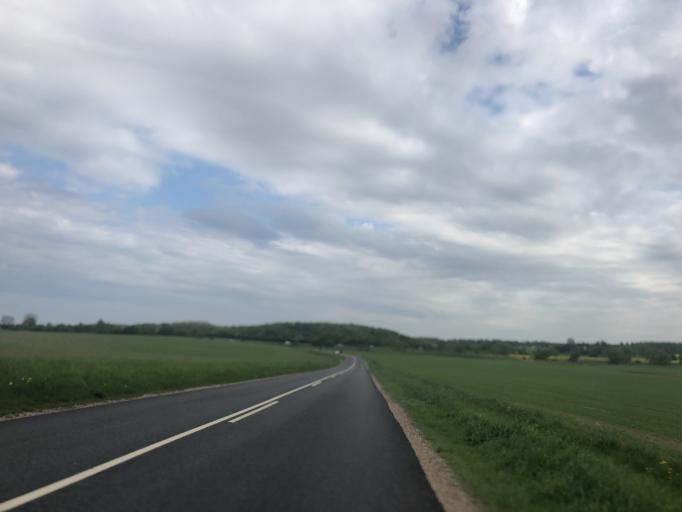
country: DK
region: Zealand
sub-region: Koge Kommune
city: Ejby
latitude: 55.4730
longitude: 12.1174
